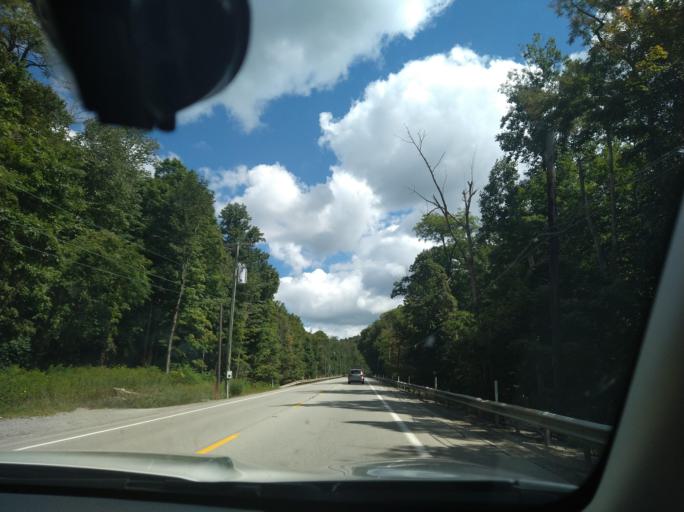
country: US
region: Pennsylvania
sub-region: Fayette County
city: Bear Rocks
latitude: 40.0738
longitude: -79.2990
